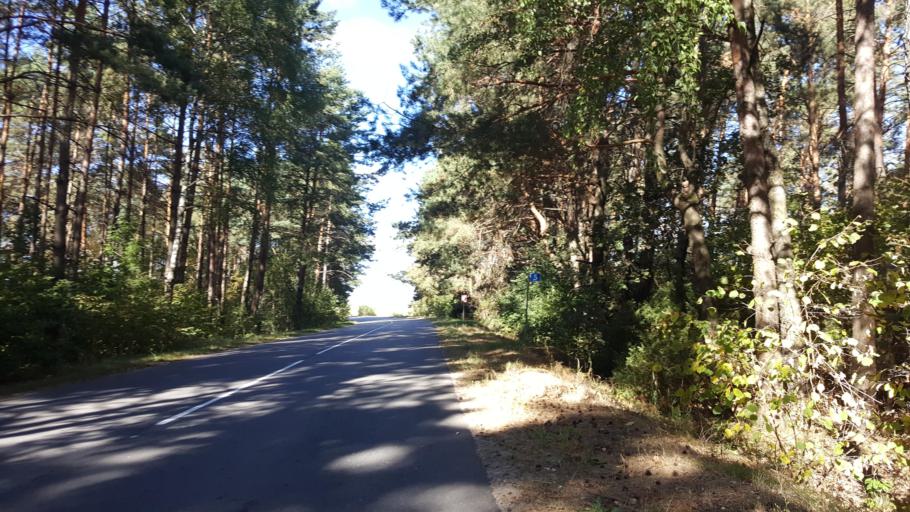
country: BY
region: Brest
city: Kamyanyets
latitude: 52.3801
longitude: 23.6841
